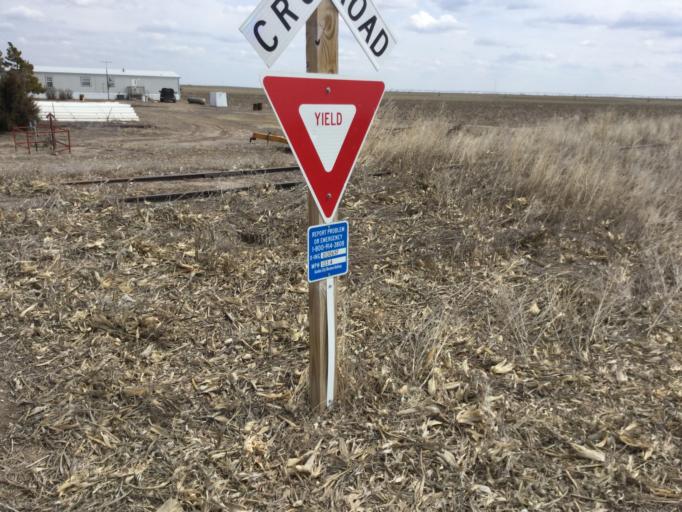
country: US
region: Kansas
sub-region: Scott County
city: Scott City
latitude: 38.2940
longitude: -100.9144
